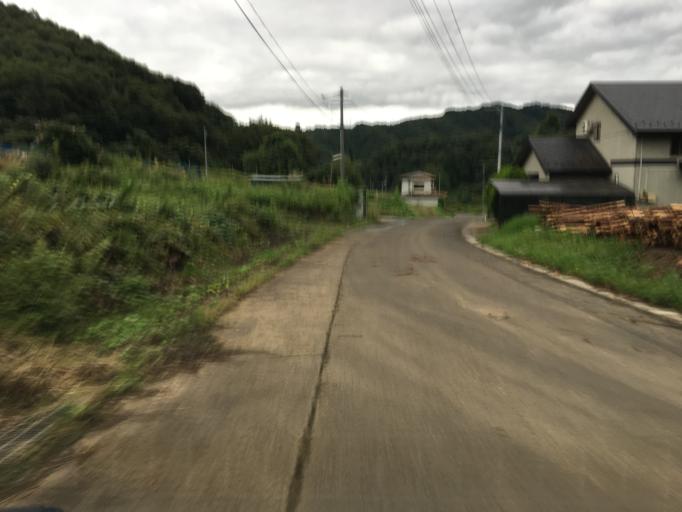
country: JP
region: Fukushima
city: Hobaramachi
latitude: 37.7605
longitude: 140.5403
